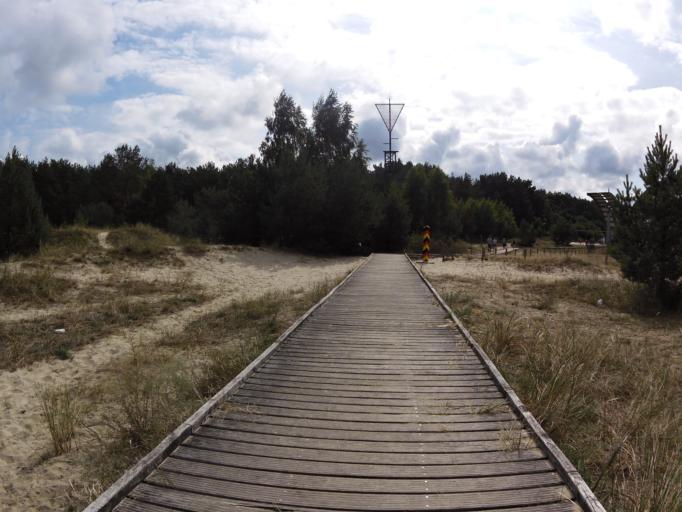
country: PL
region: West Pomeranian Voivodeship
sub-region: Swinoujscie
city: Swinoujscie
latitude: 53.9280
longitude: 14.2262
